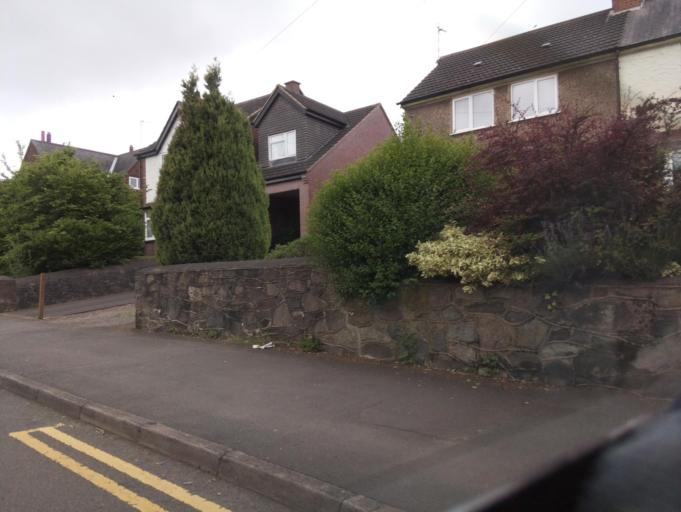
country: GB
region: England
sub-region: Leicestershire
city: Coalville
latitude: 52.7392
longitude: -1.3544
